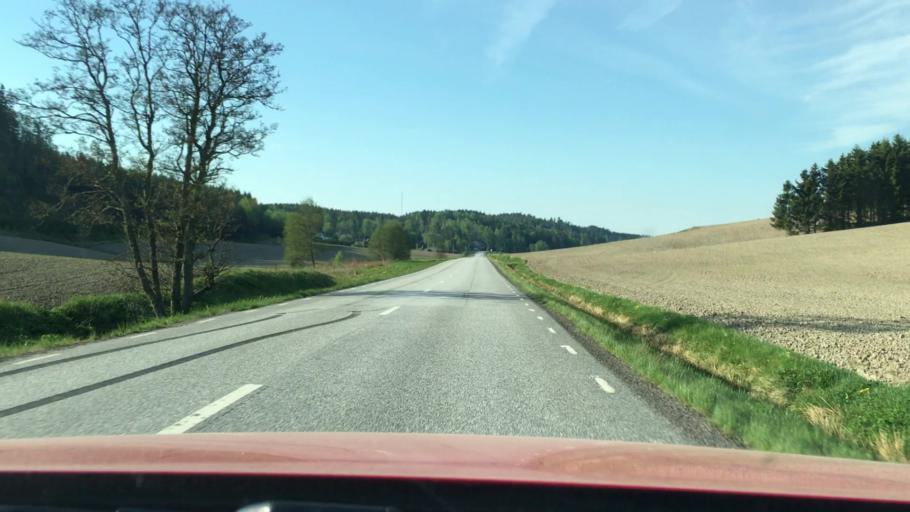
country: SE
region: Vaestra Goetaland
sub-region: Munkedals Kommun
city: Munkedal
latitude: 58.6116
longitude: 11.5588
